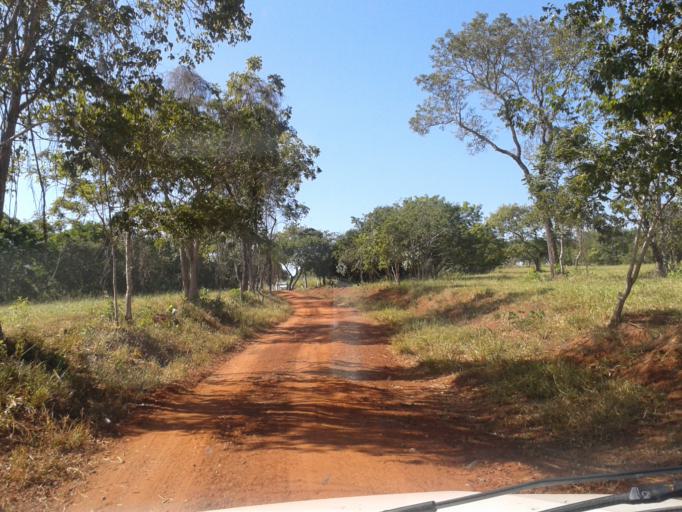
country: BR
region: Minas Gerais
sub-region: Campina Verde
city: Campina Verde
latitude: -19.3863
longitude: -49.7518
